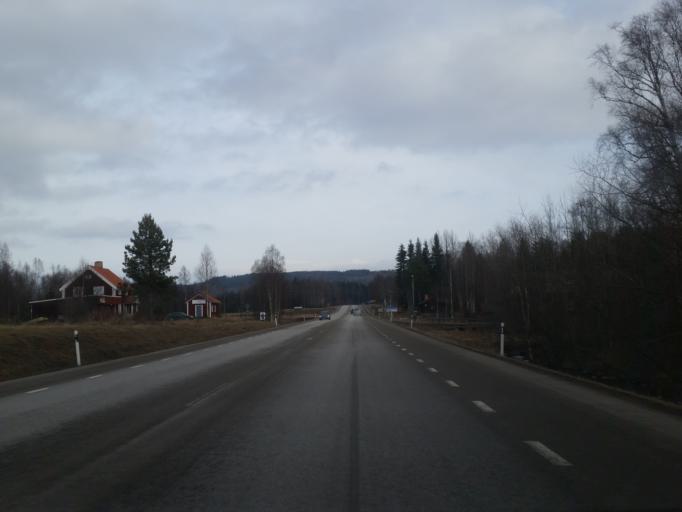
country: SE
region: Dalarna
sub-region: Leksand Municipality
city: Leksand
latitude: 60.7769
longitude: 15.0215
